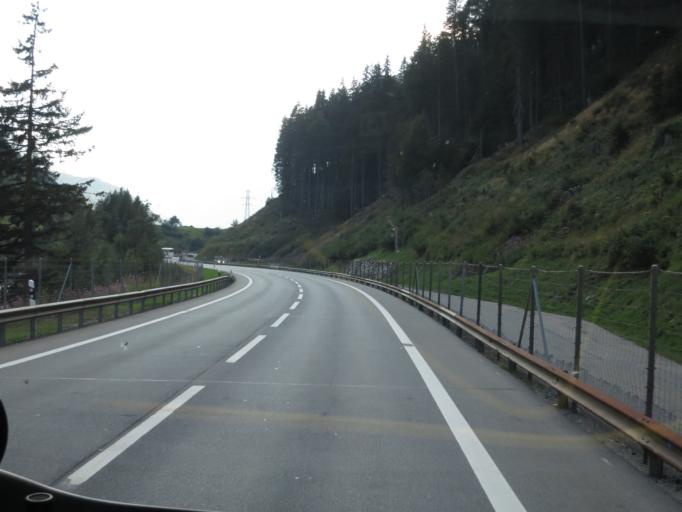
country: CH
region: Grisons
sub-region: Hinterrhein District
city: Hinterrhein
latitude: 46.5325
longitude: 9.2142
